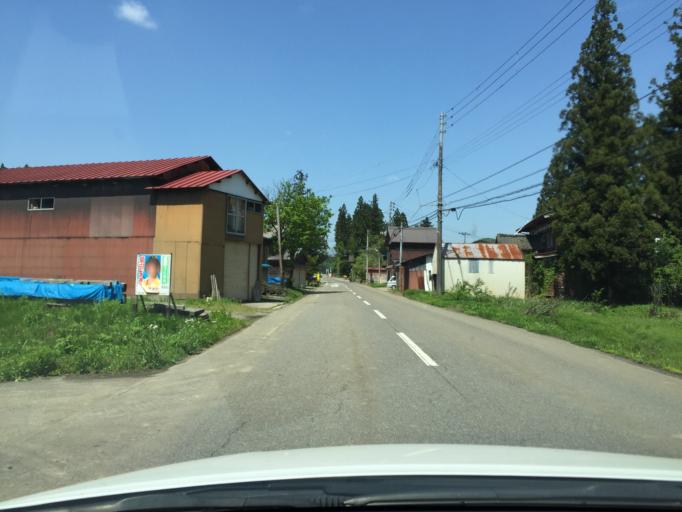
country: JP
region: Niigata
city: Tochio-honcho
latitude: 37.5046
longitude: 139.0639
